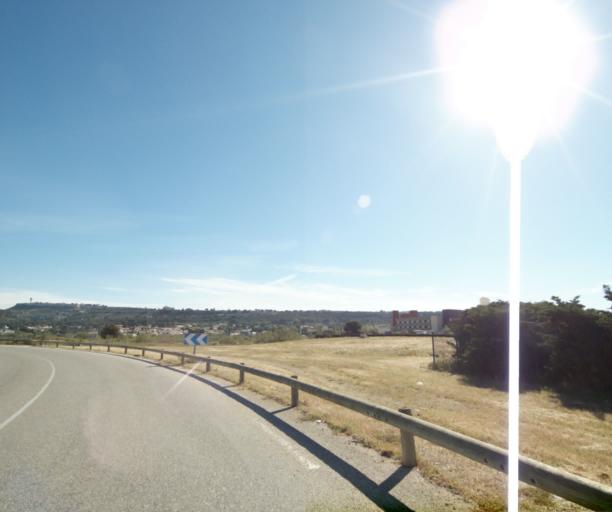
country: FR
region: Provence-Alpes-Cote d'Azur
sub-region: Departement des Bouches-du-Rhone
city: Vitrolles
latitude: 43.4466
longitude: 5.2252
